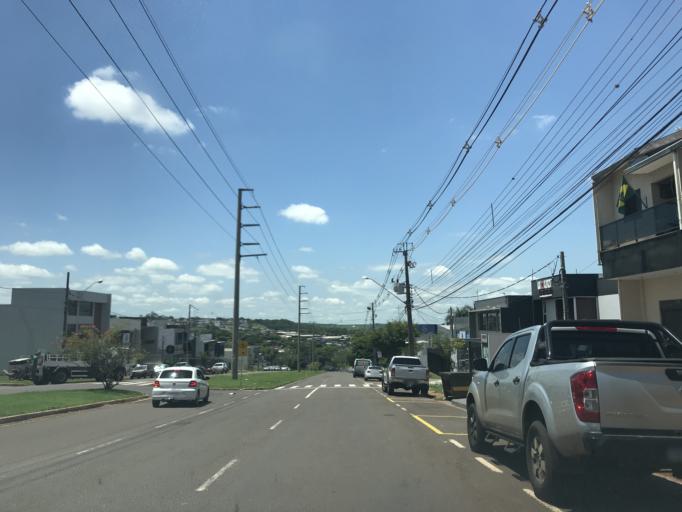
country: BR
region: Parana
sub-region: Maringa
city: Maringa
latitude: -23.4503
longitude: -51.9326
